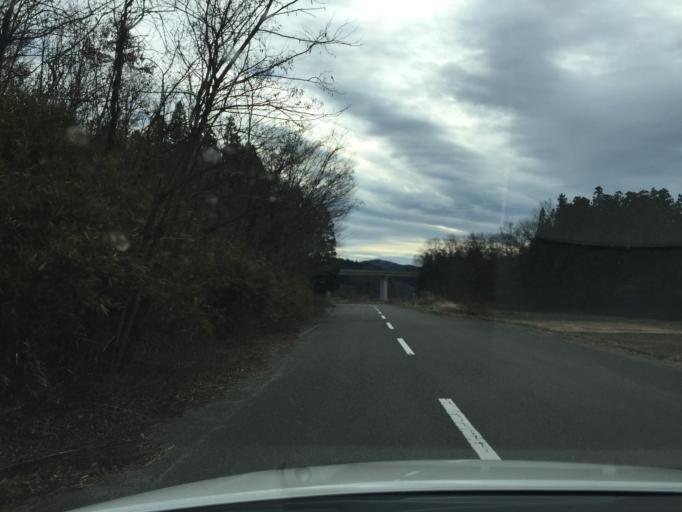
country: JP
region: Fukushima
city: Funehikimachi-funehiki
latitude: 37.2957
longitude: 140.6056
